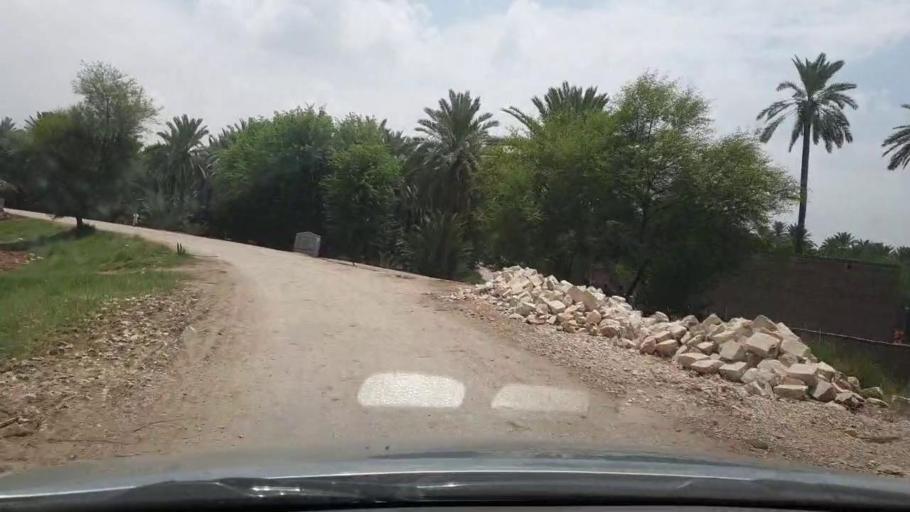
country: PK
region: Sindh
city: Khairpur
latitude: 27.4331
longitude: 68.7674
